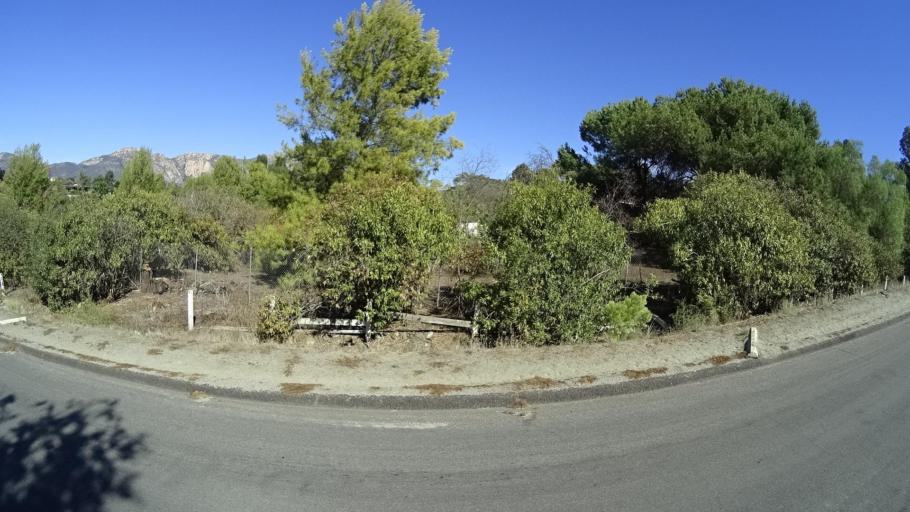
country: US
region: California
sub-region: San Diego County
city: Harbison Canyon
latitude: 32.8645
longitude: -116.8611
